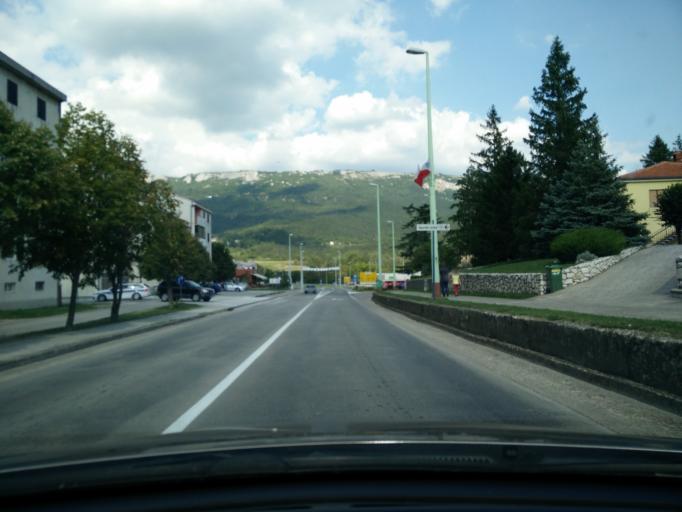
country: HR
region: Istarska
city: Buzet
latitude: 45.4096
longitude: 13.9686
